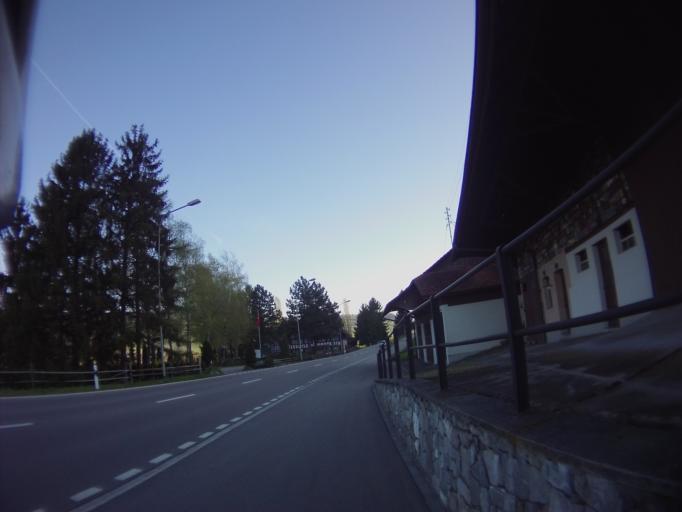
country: CH
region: Zurich
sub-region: Bezirk Affoltern
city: Hedingen
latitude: 47.3054
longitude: 8.4501
